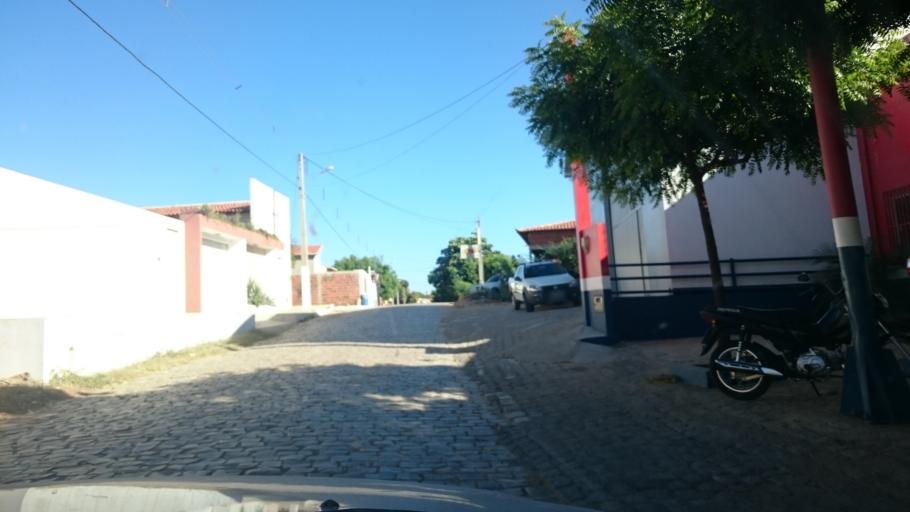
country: BR
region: Paraiba
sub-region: Catole Do Rocha
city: Sao Bento
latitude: -6.1589
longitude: -37.7645
